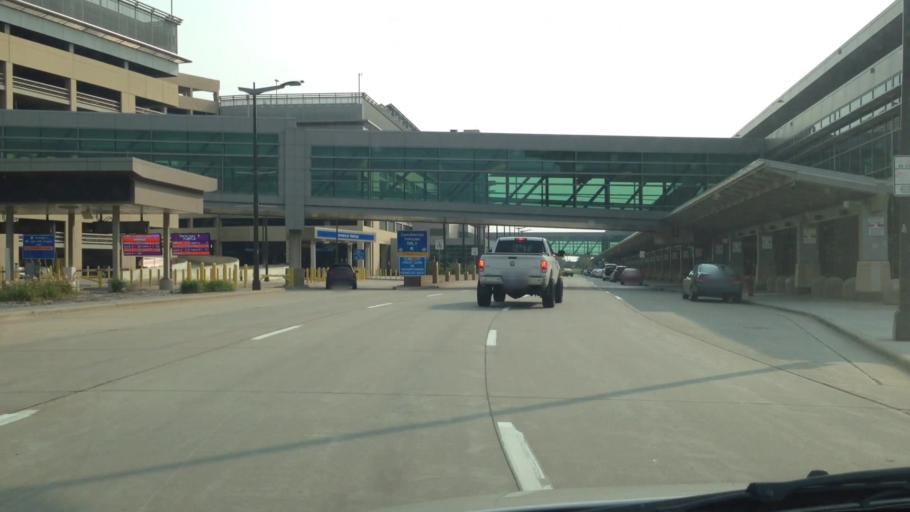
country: US
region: Minnesota
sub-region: Hennepin County
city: Richfield
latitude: 44.8753
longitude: -93.2256
